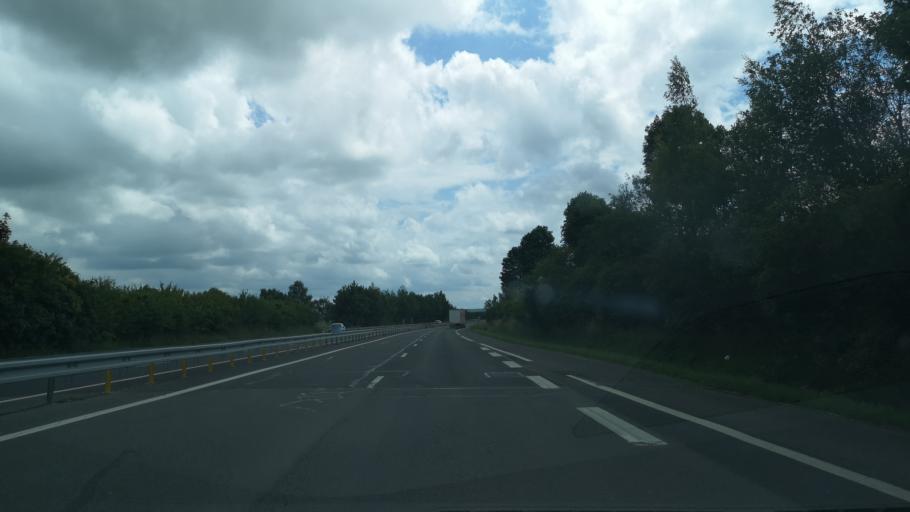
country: FR
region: Champagne-Ardenne
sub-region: Departement des Ardennes
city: Chateau-Porcien
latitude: 49.4360
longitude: 4.2796
